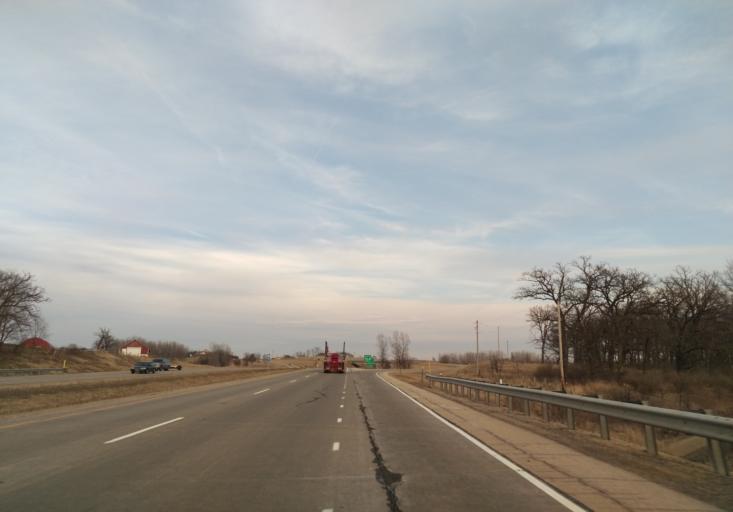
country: US
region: Wisconsin
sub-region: Dane County
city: Verona
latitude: 42.9867
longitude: -89.5681
